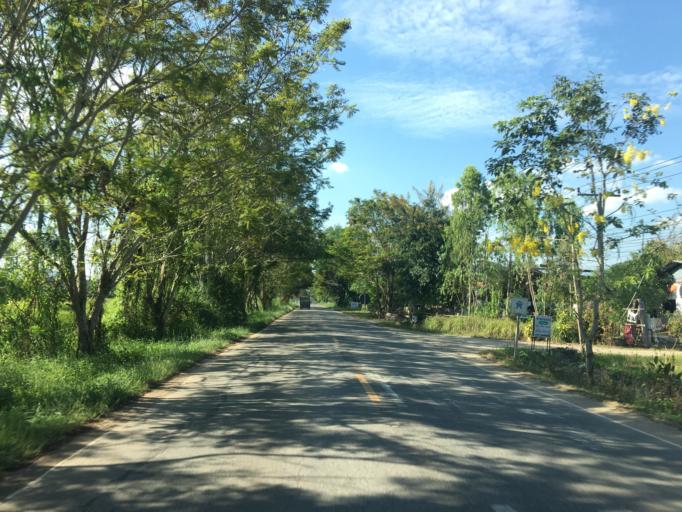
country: TH
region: Phayao
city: Chun
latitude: 19.3289
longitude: 100.1424
